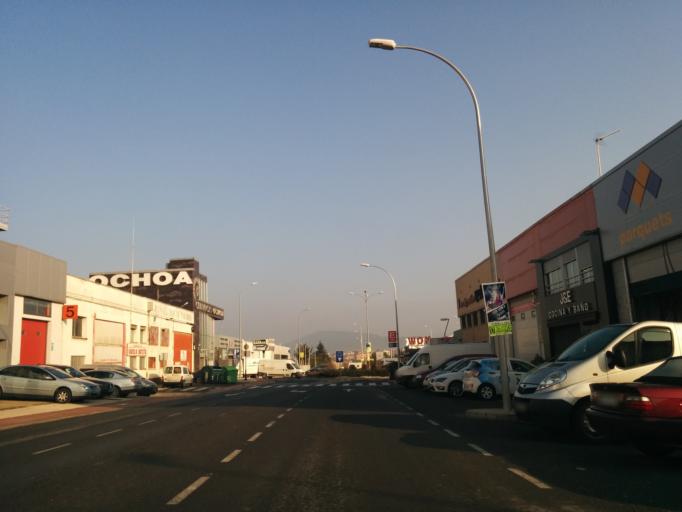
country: ES
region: Navarre
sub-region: Provincia de Navarra
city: Segundo Ensanche
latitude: 42.7875
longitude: -1.6256
